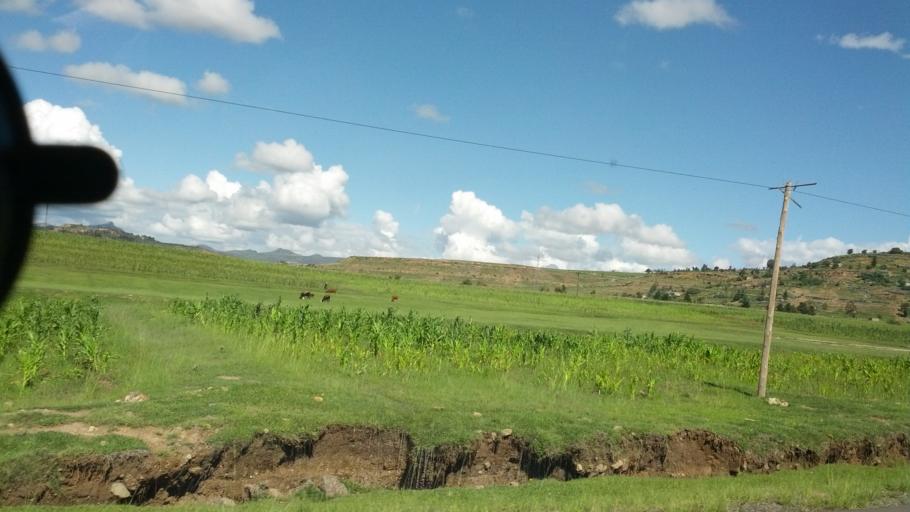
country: LS
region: Maseru
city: Maseru
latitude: -29.5839
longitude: 27.4957
